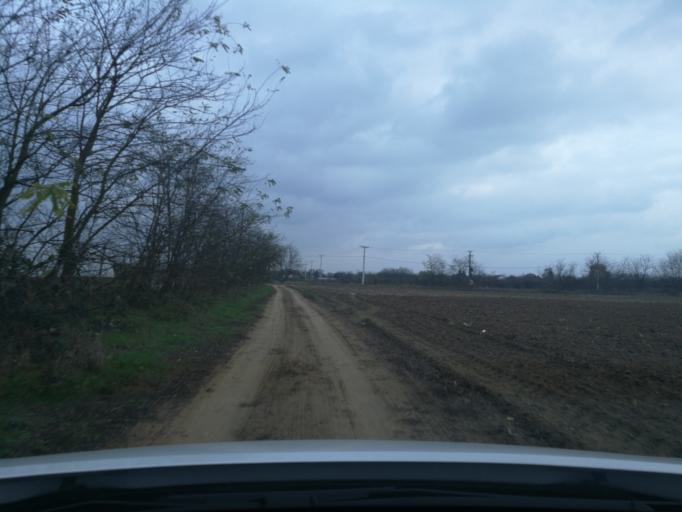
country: HU
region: Szabolcs-Szatmar-Bereg
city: Nyirpazony
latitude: 47.9709
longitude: 21.7944
